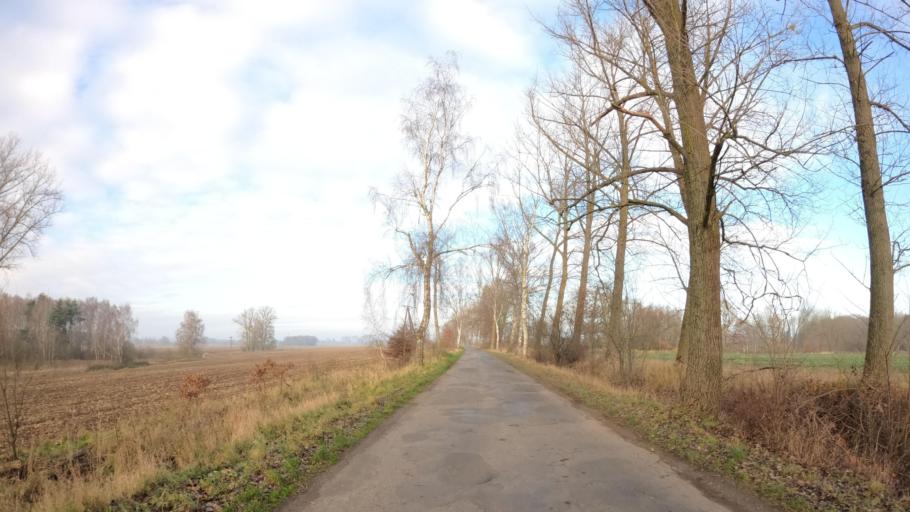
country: PL
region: West Pomeranian Voivodeship
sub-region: Powiat goleniowski
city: Maszewo
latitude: 53.5656
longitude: 15.0904
